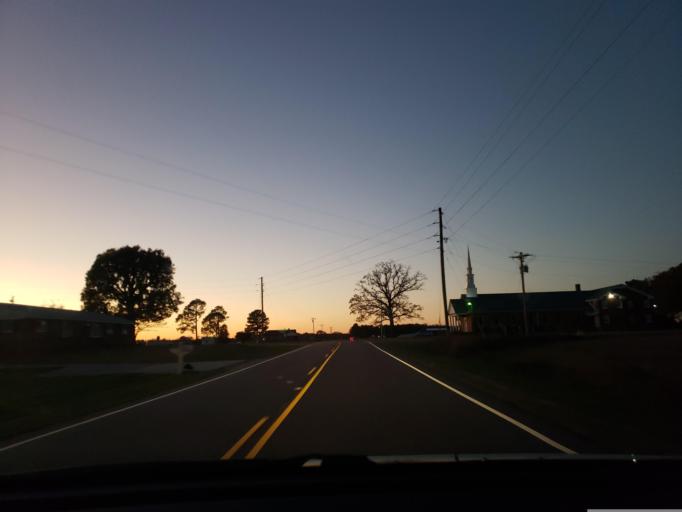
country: US
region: North Carolina
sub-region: Duplin County
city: Kenansville
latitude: 34.9032
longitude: -77.9184
